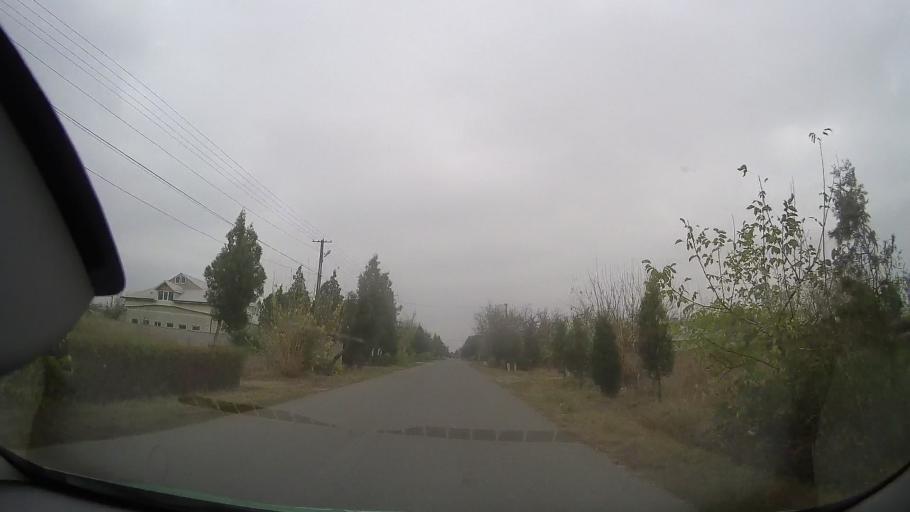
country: RO
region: Buzau
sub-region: Comuna Scutelnici
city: Scutelnici
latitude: 44.8489
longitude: 26.9147
